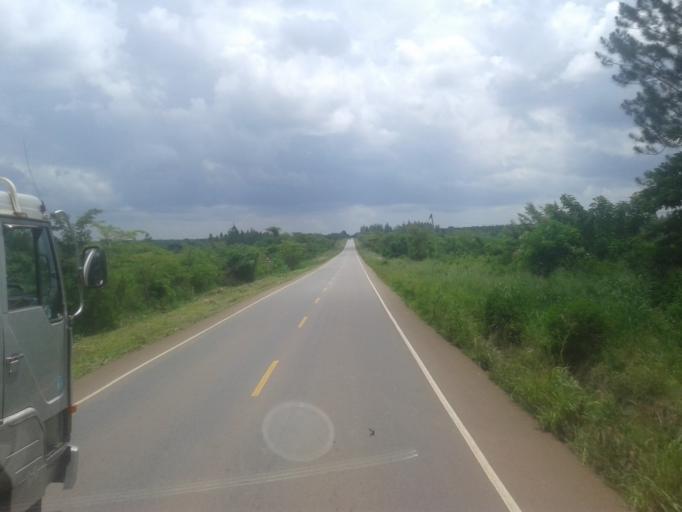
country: UG
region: Central Region
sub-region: Nakasongola District
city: Nakasongola
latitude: 1.1995
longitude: 32.4626
